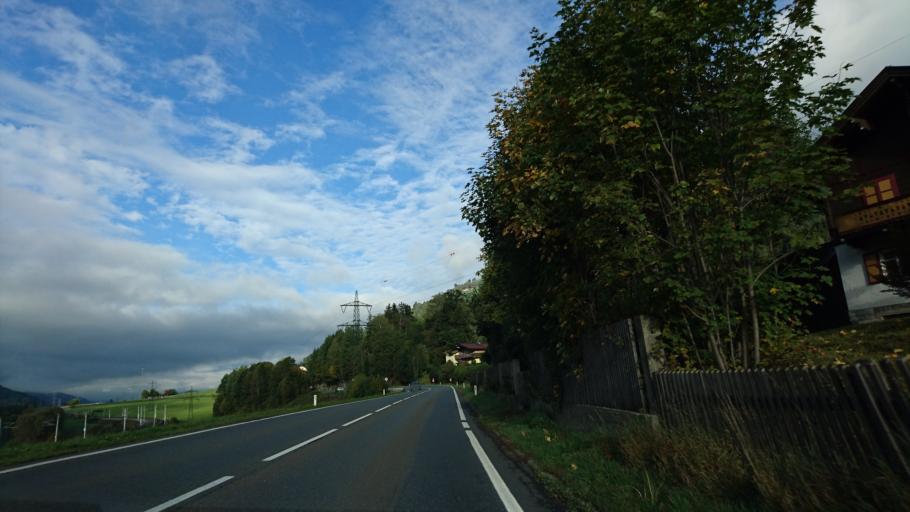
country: AT
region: Salzburg
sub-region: Politischer Bezirk Zell am See
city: Bruck an der Grossglocknerstrasse
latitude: 47.2845
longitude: 12.8584
